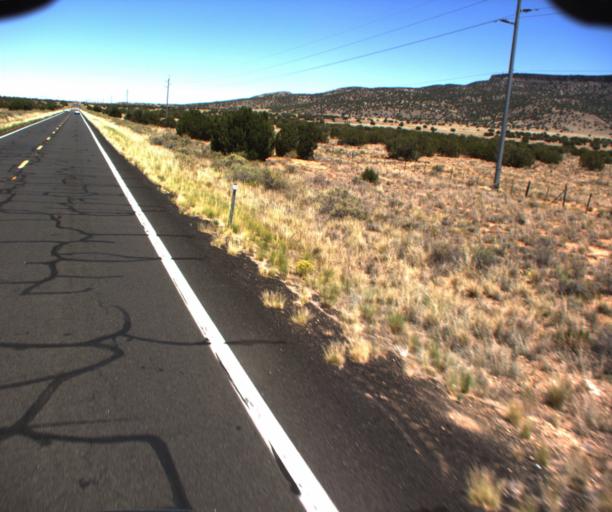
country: US
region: Arizona
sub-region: Coconino County
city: LeChee
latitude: 34.8438
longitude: -110.9356
